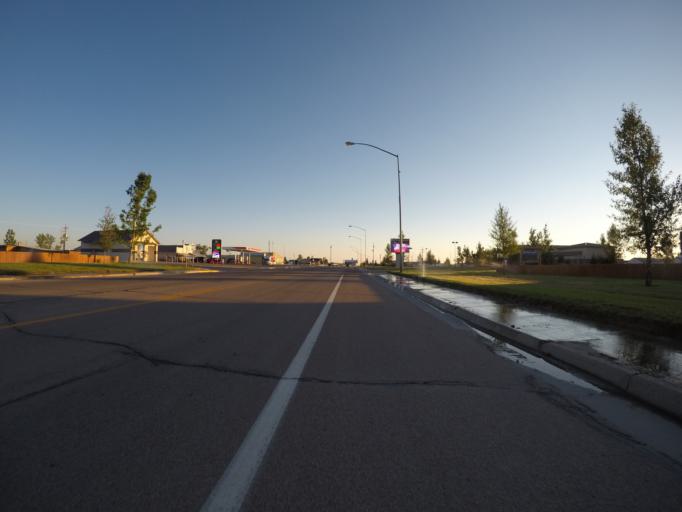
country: US
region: Wyoming
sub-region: Sublette County
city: Marbleton
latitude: 42.5530
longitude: -110.1095
